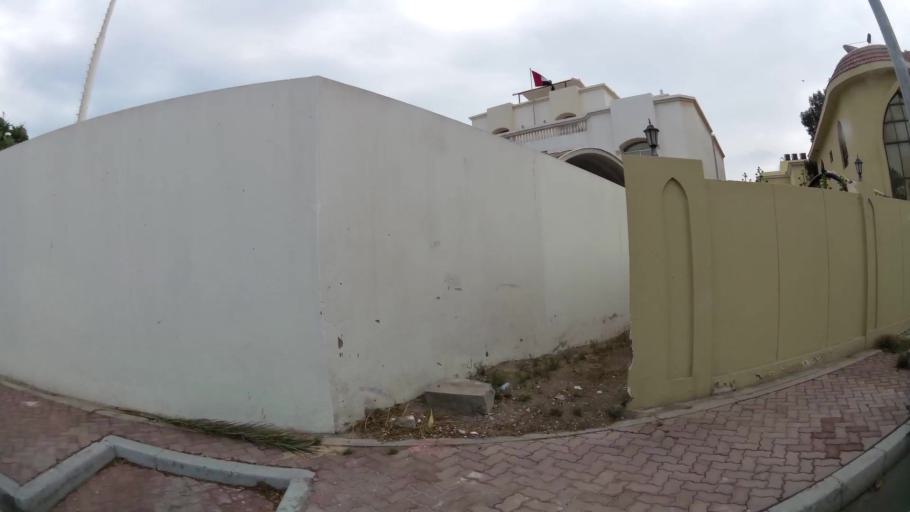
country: AE
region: Abu Dhabi
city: Abu Dhabi
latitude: 24.4372
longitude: 54.3814
